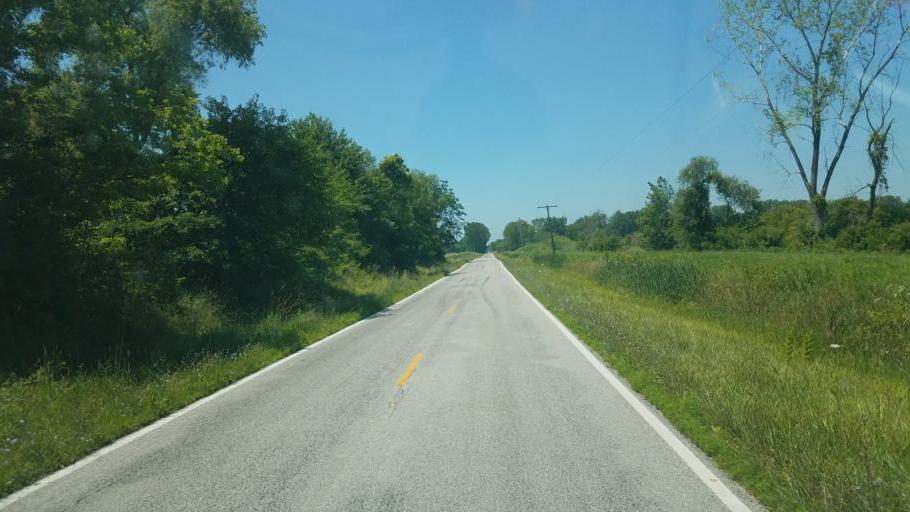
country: US
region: Ohio
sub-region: Ottawa County
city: Port Clinton
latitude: 41.4223
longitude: -83.0141
